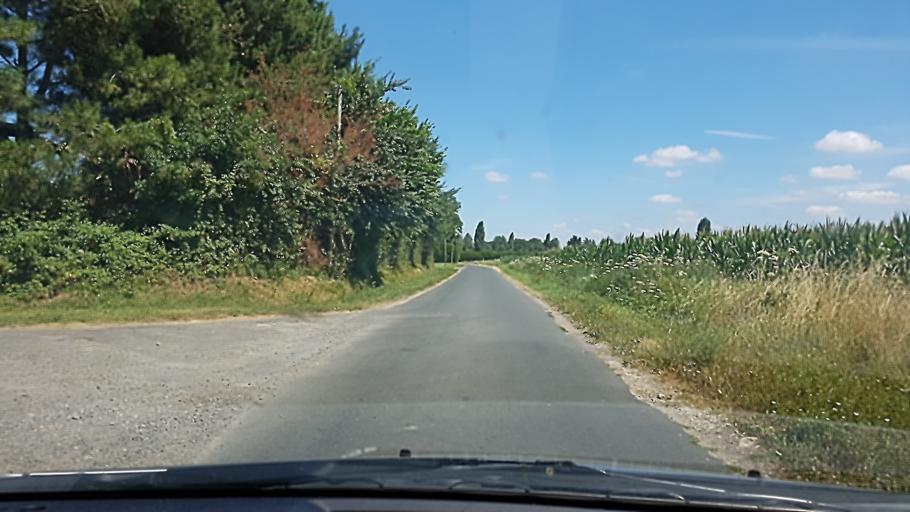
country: FR
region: Pays de la Loire
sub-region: Departement de Maine-et-Loire
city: Le Plessis-Grammoire
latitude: 47.5204
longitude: -0.4046
